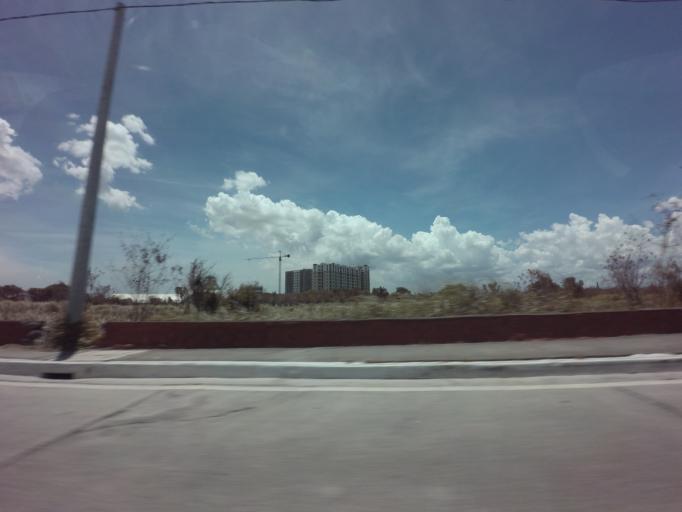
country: PH
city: Sambayanihan People's Village
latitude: 14.4864
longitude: 120.9953
